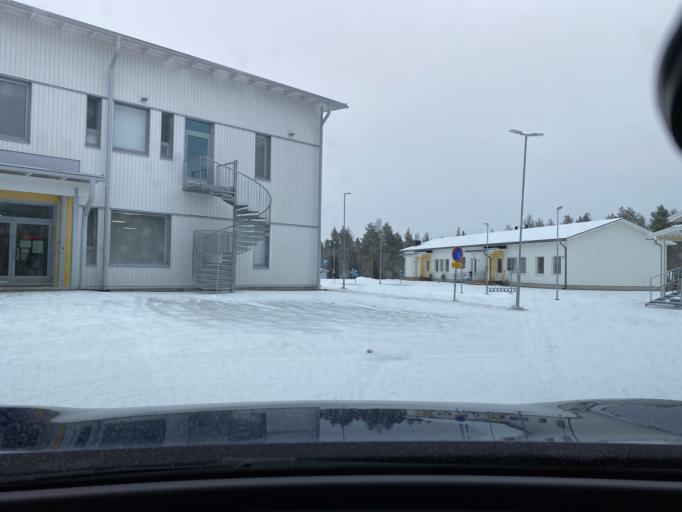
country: FI
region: Lapland
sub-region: Rovaniemi
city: Ranua
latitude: 65.9247
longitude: 26.5167
